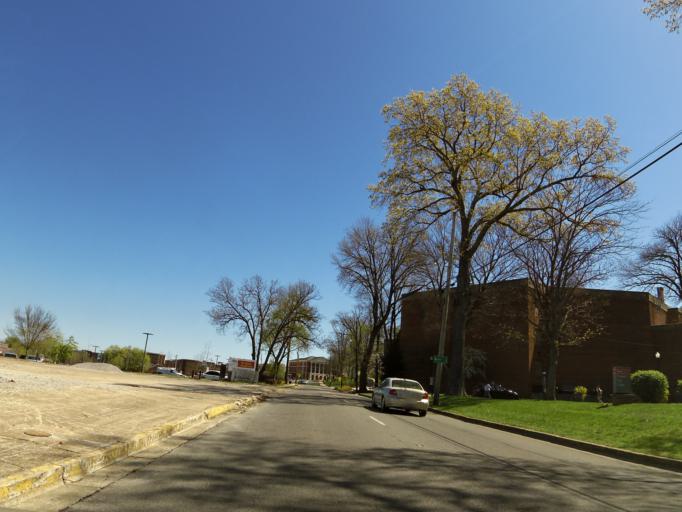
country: US
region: Kentucky
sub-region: Warren County
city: Bowling Green
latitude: 36.9891
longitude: -86.4557
